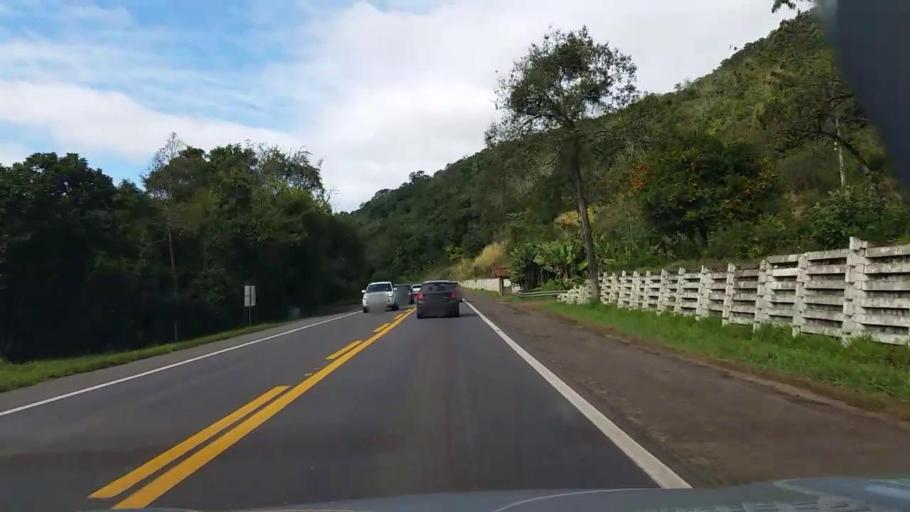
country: BR
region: Rio Grande do Sul
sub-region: Arroio Do Meio
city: Arroio do Meio
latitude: -29.3347
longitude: -52.0953
